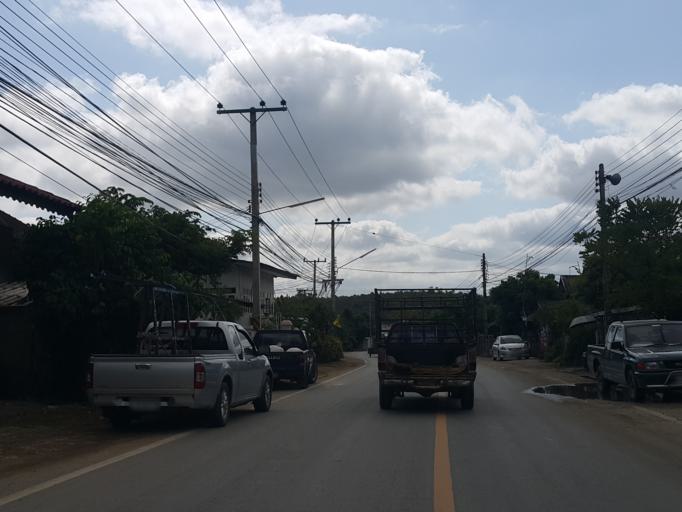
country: TH
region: Lamphun
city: Ban Thi
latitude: 18.6128
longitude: 99.0914
